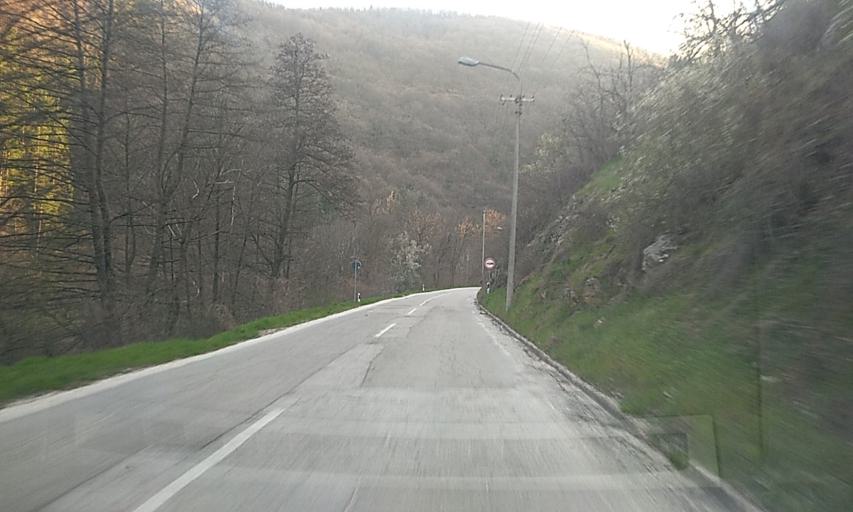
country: RS
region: Central Serbia
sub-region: Pcinjski Okrug
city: Bosilegrad
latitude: 42.4981
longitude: 22.4652
